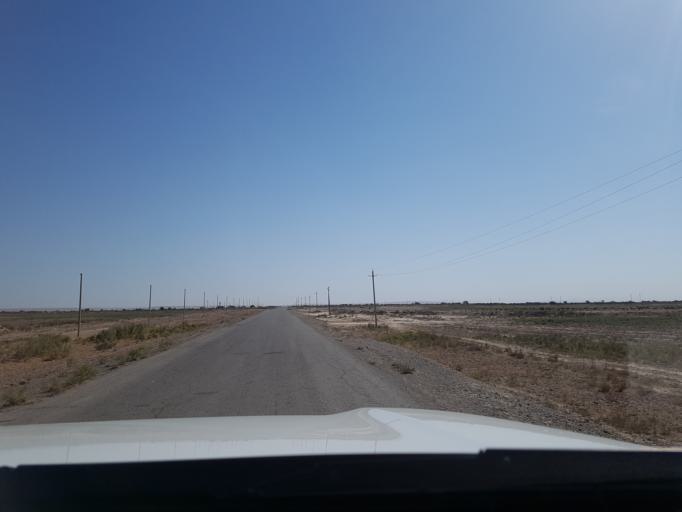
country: IR
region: Razavi Khorasan
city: Sarakhs
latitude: 36.5027
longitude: 61.2535
